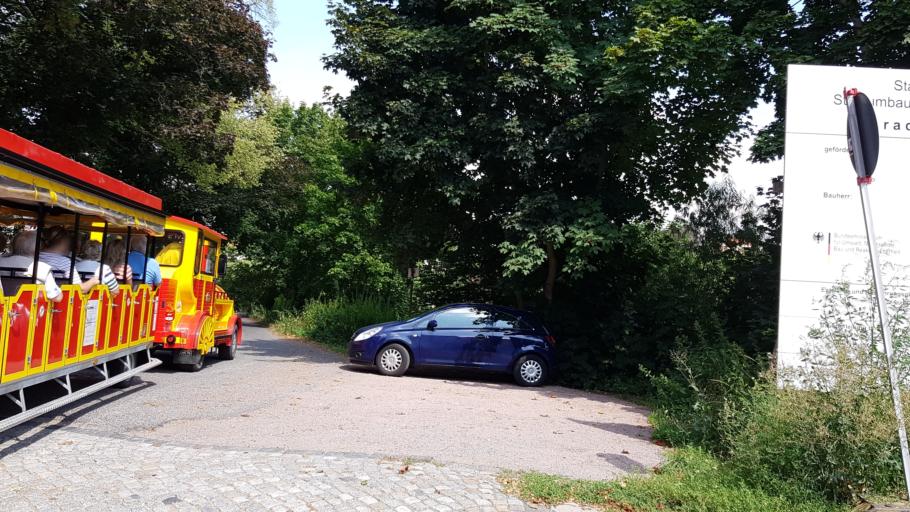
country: DE
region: Saxony
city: Frankenberg
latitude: 50.9083
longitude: 13.0359
